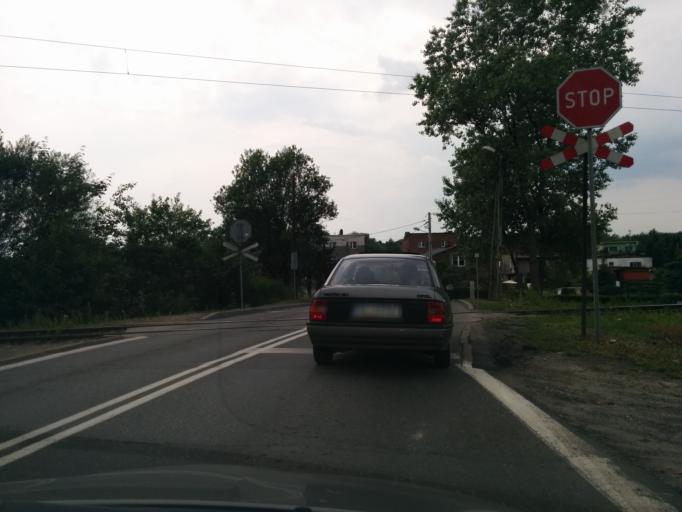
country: PL
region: Silesian Voivodeship
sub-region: Ruda Slaska
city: Ruda Slaska
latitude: 50.2552
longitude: 18.8415
